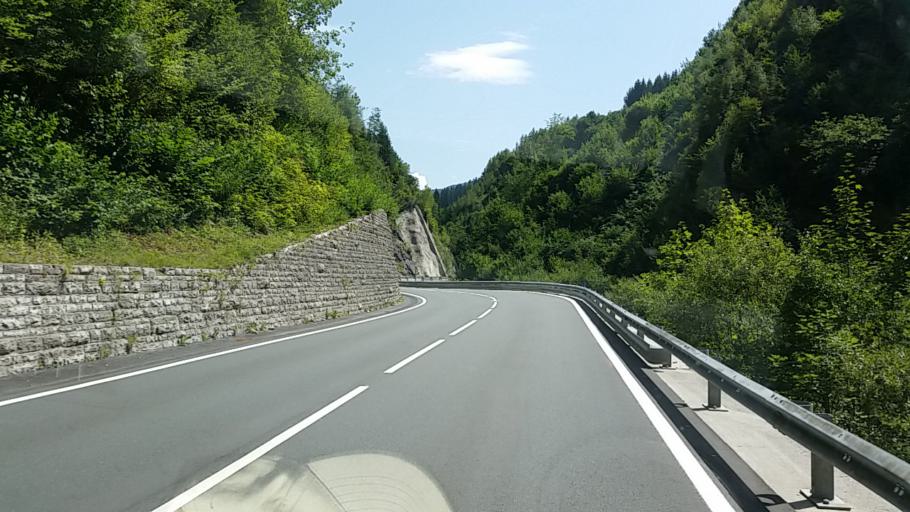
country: AT
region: Salzburg
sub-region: Politischer Bezirk Sankt Johann im Pongau
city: Bischofshofen
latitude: 47.4364
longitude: 13.2255
